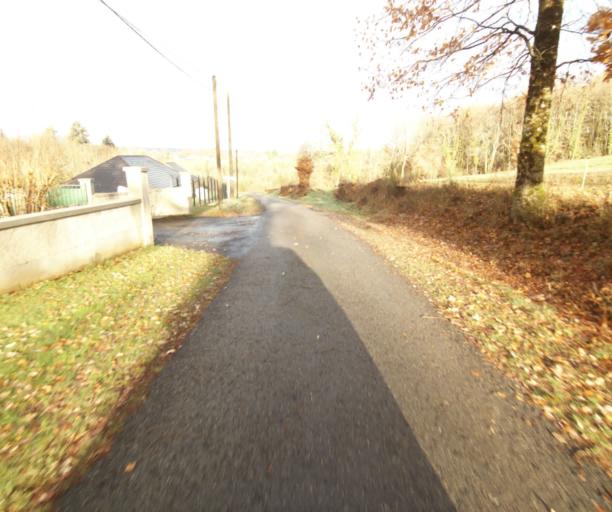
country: FR
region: Limousin
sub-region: Departement de la Correze
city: Saint-Mexant
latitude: 45.2597
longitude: 1.6283
